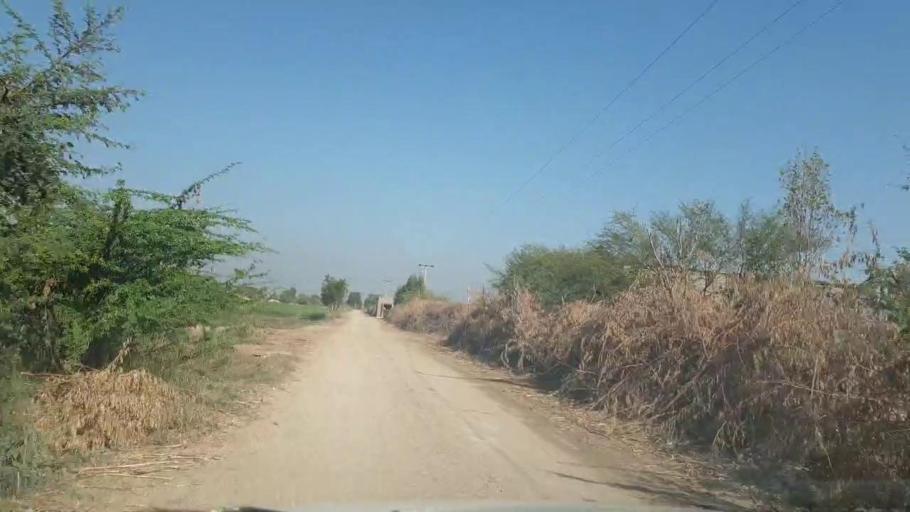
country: PK
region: Sindh
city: Mirpur Khas
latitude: 25.5039
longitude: 69.1584
